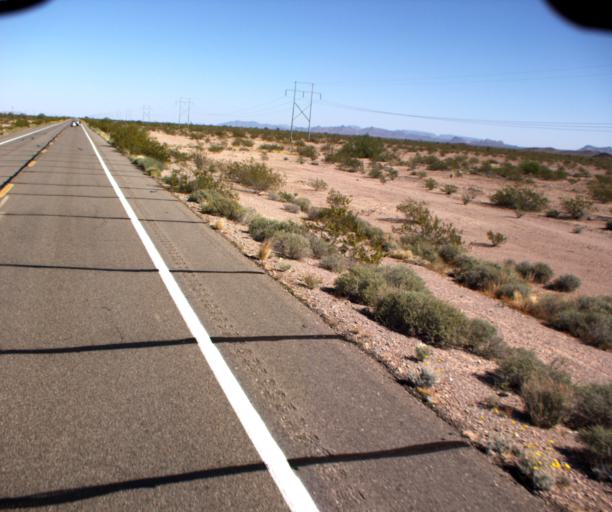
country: US
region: Arizona
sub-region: La Paz County
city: Quartzsite
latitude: 33.3201
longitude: -114.2169
